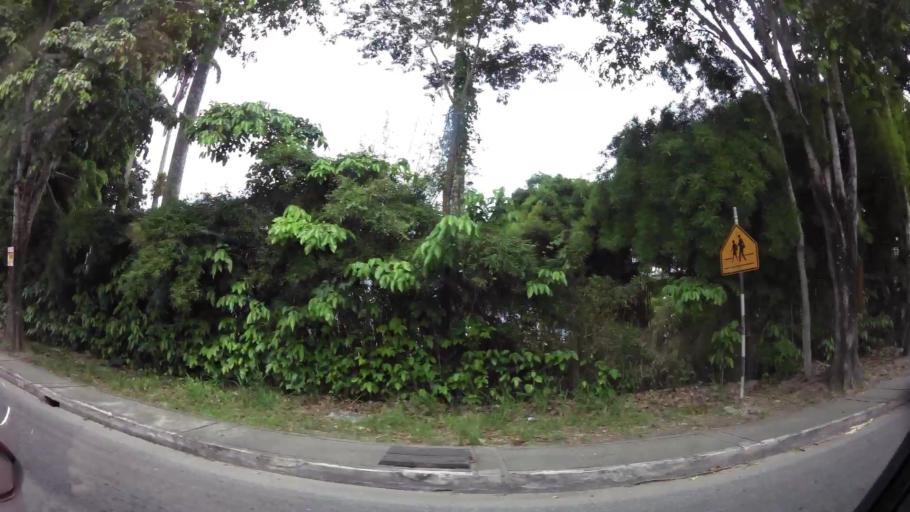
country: TT
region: Couva-Tabaquite-Talparo
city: Couva
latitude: 10.4220
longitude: -61.4619
